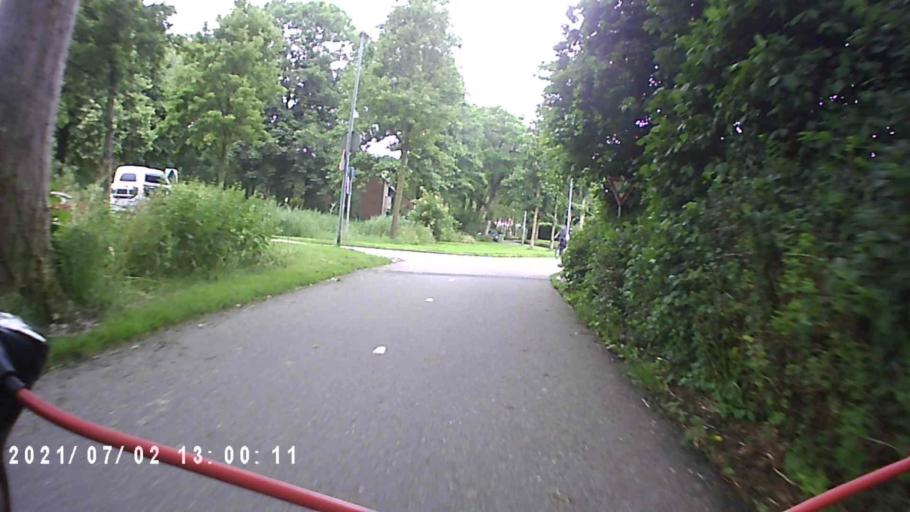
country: NL
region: Groningen
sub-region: Gemeente Groningen
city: Oosterpark
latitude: 53.2426
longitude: 6.5923
